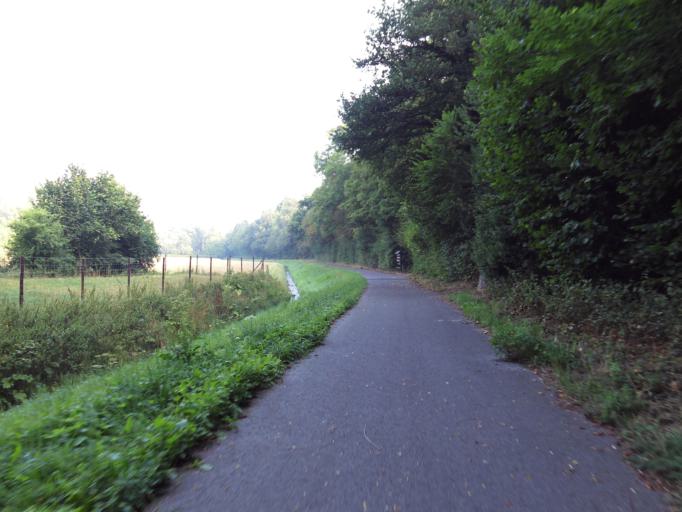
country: DE
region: North Rhine-Westphalia
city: Geilenkirchen
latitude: 50.9856
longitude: 6.1889
